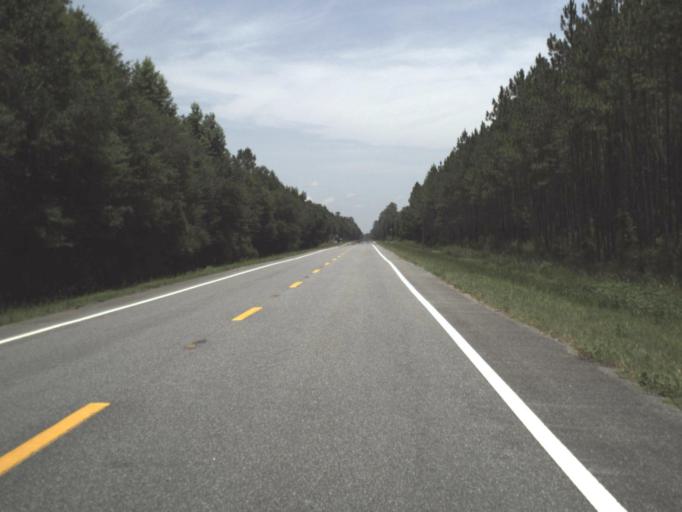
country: US
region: Florida
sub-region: Taylor County
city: Steinhatchee
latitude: 29.8274
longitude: -83.3146
